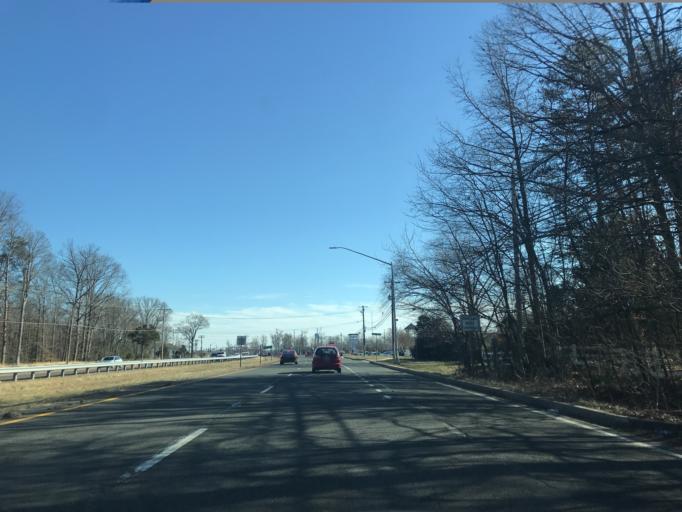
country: US
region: Maryland
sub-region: Charles County
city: Waldorf
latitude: 38.6323
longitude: -76.9209
